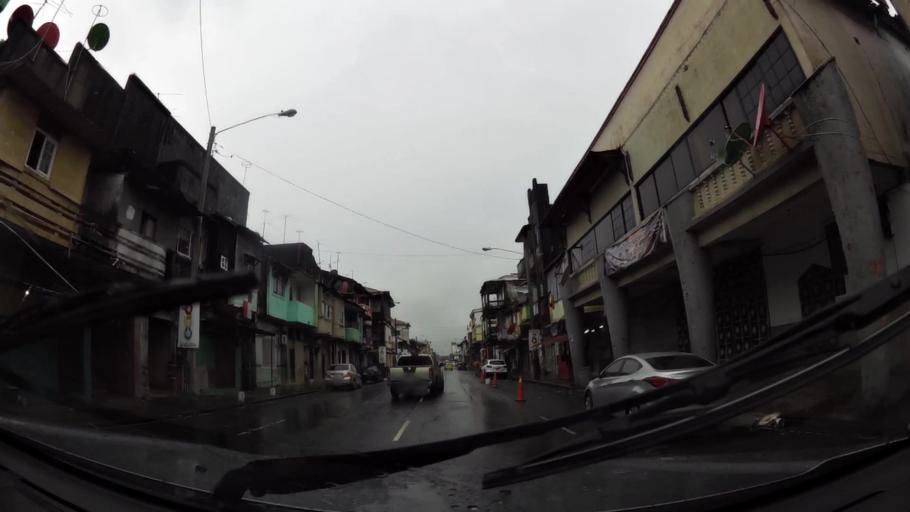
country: PA
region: Colon
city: Colon
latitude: 9.3591
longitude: -79.9033
